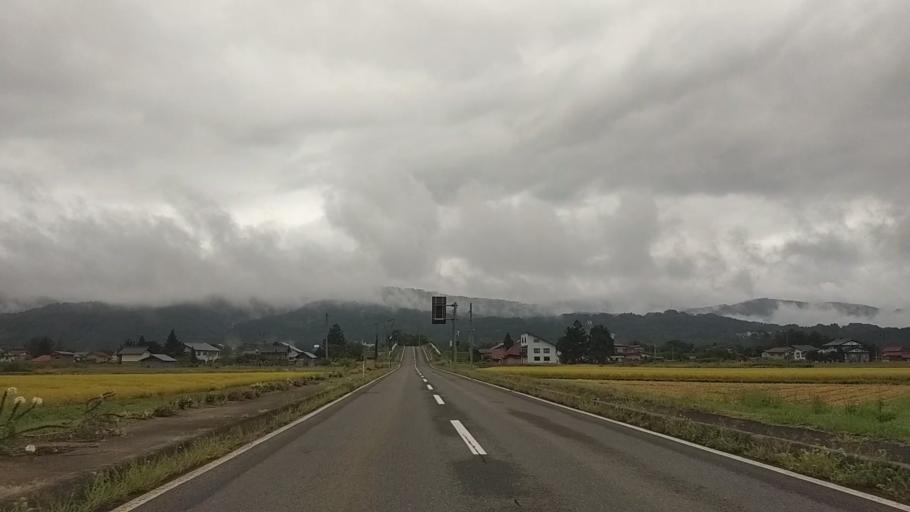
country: JP
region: Nagano
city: Iiyama
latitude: 36.8446
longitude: 138.3739
